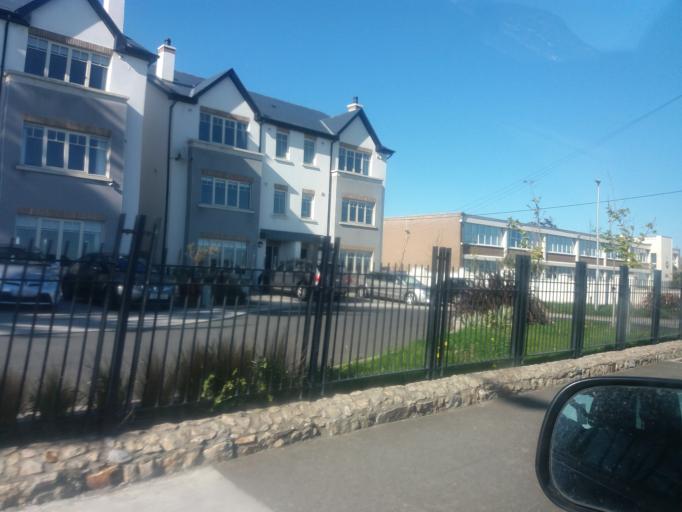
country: IE
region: Leinster
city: Sutton
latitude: 53.3890
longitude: -6.1190
